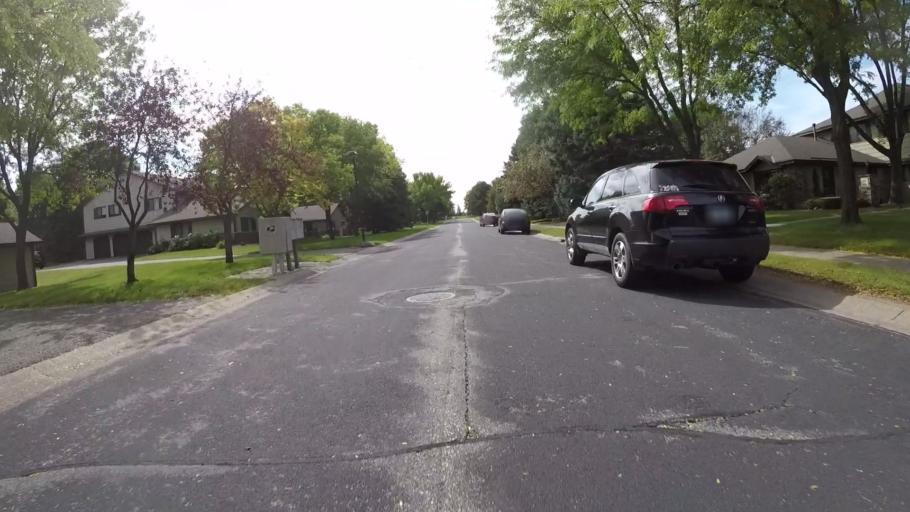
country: US
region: Minnesota
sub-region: Hennepin County
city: Eden Prairie
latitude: 44.8678
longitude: -93.4492
